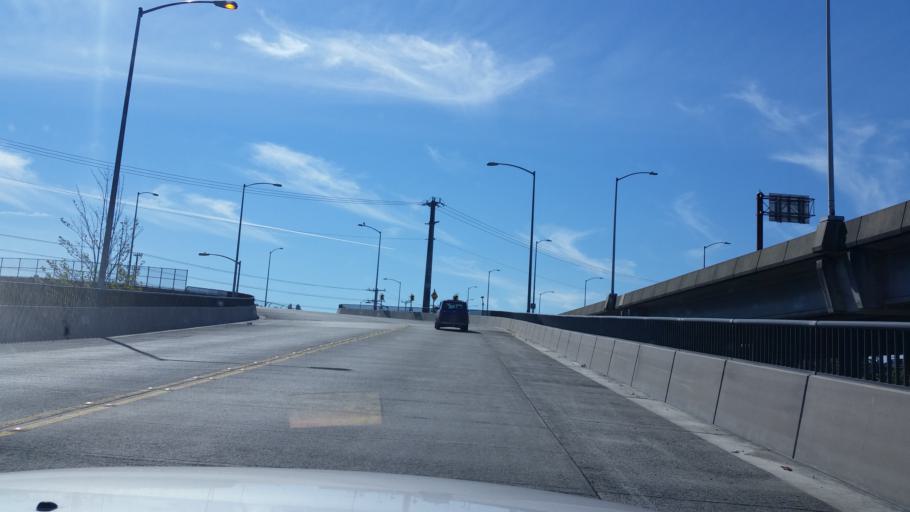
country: US
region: Washington
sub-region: King County
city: Seattle
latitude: 47.5711
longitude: -122.3404
